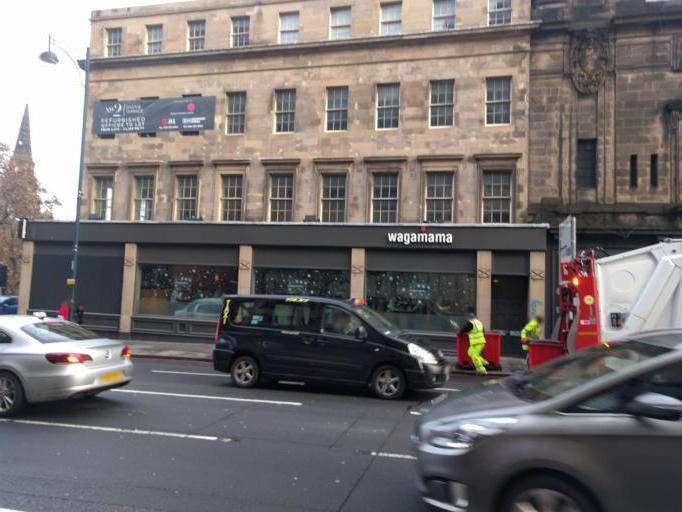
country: GB
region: Scotland
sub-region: Edinburgh
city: Edinburgh
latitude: 55.9484
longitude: -3.2066
